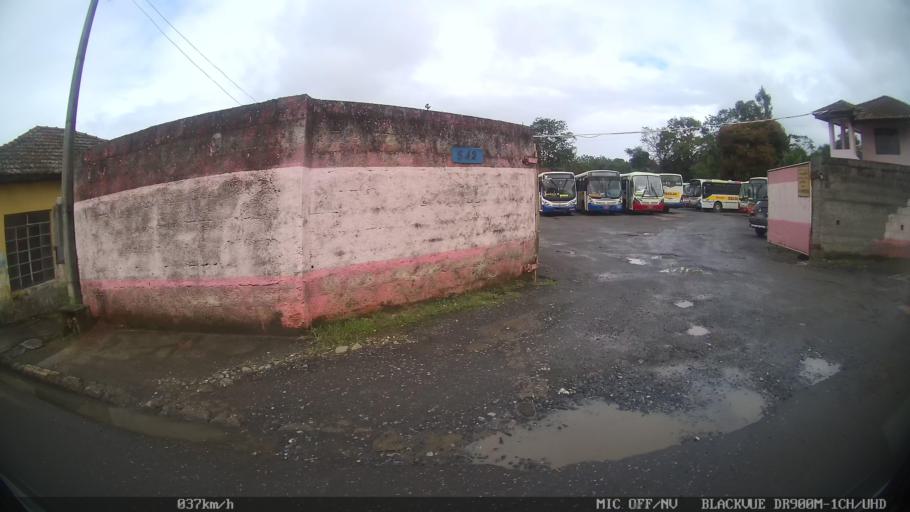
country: BR
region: Sao Paulo
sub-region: Cajati
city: Cajati
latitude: -24.7254
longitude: -48.1047
